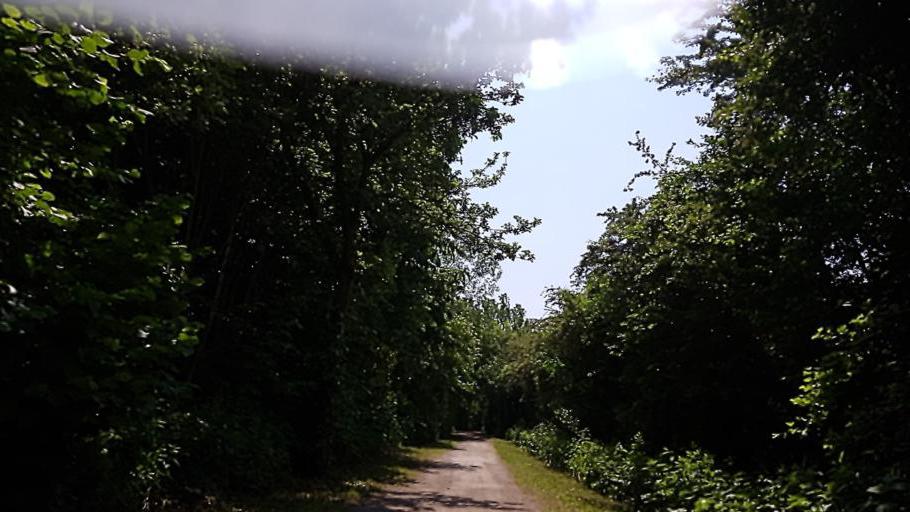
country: FR
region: Nord-Pas-de-Calais
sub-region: Departement du Nord
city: Vieux-Conde
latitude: 50.4808
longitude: 3.5708
